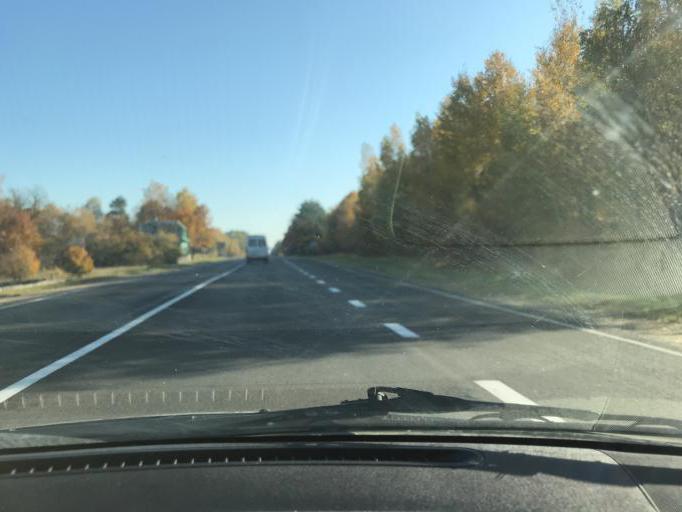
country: BY
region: Brest
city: Lyakhavichy
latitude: 52.9583
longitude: 26.3516
